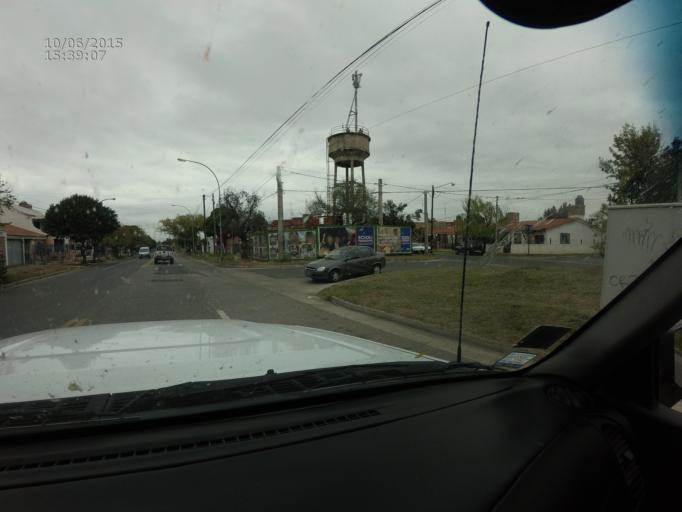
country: AR
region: Cordoba
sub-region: Departamento de Capital
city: Cordoba
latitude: -31.3618
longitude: -64.2262
